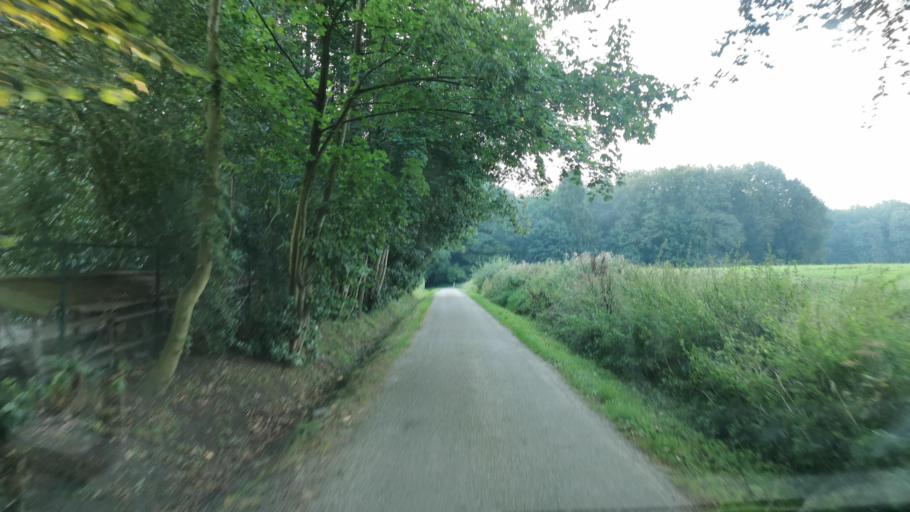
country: NL
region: Overijssel
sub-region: Gemeente Oldenzaal
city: Oldenzaal
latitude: 52.3018
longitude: 6.9507
